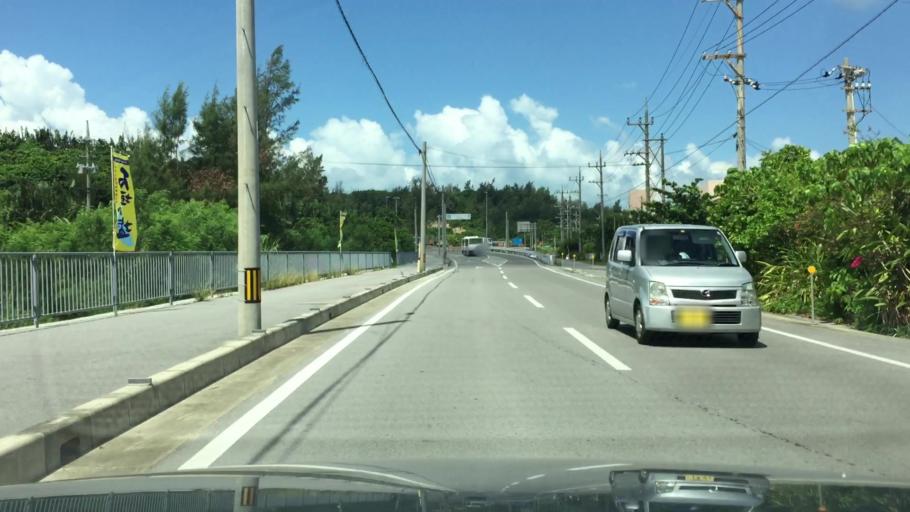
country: JP
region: Okinawa
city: Ishigaki
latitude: 24.3777
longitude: 124.1288
